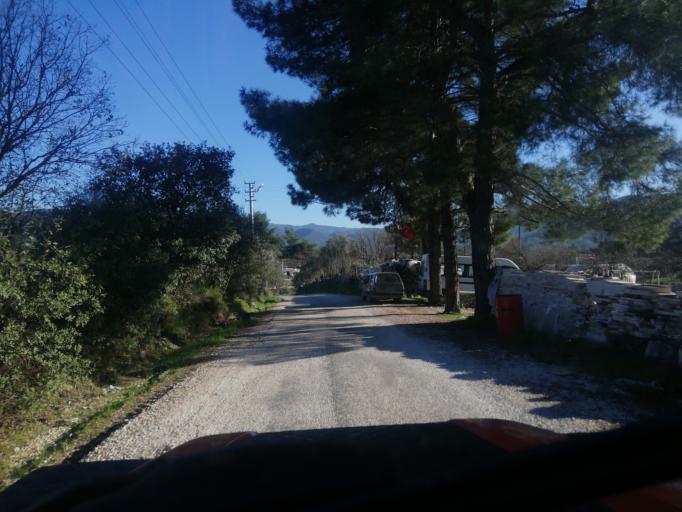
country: TR
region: Antalya
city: Kas
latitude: 36.2929
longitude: 29.7059
